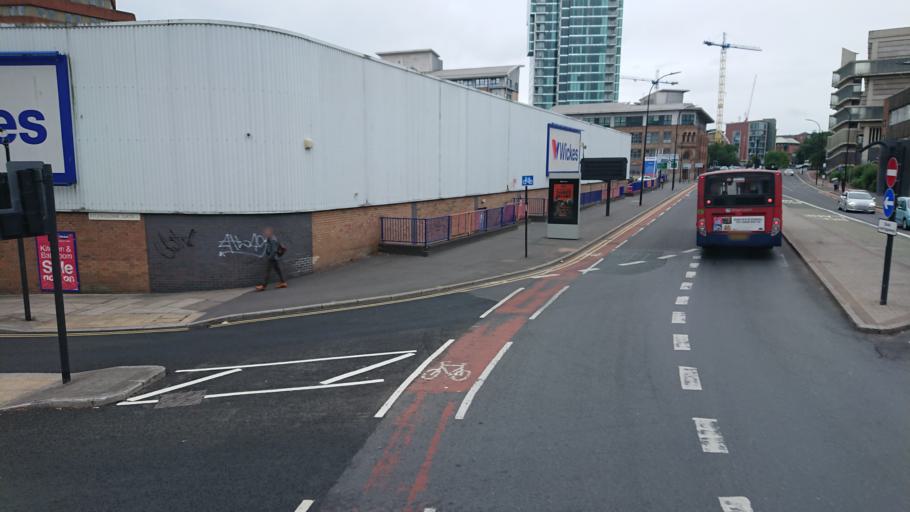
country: GB
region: England
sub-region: Sheffield
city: Sheffield
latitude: 53.3757
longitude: -1.4764
